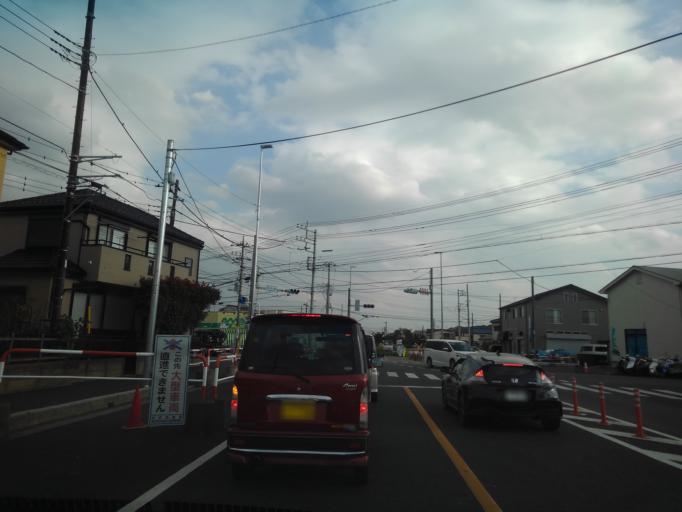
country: JP
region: Saitama
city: Tokorozawa
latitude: 35.7808
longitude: 139.4585
